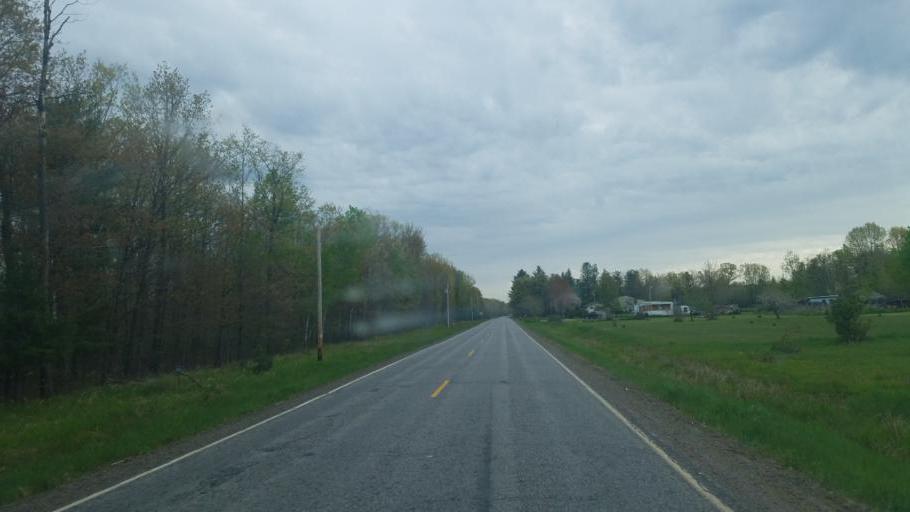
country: US
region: Wisconsin
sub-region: Wood County
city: Marshfield
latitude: 44.4025
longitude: -90.1603
